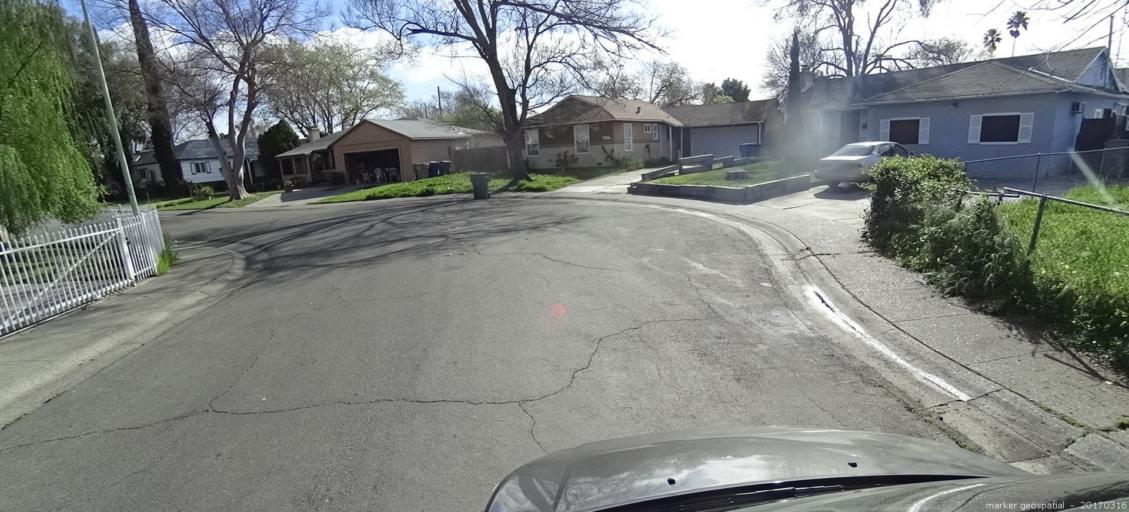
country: US
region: California
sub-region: Sacramento County
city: Parkway
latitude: 38.5105
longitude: -121.4904
